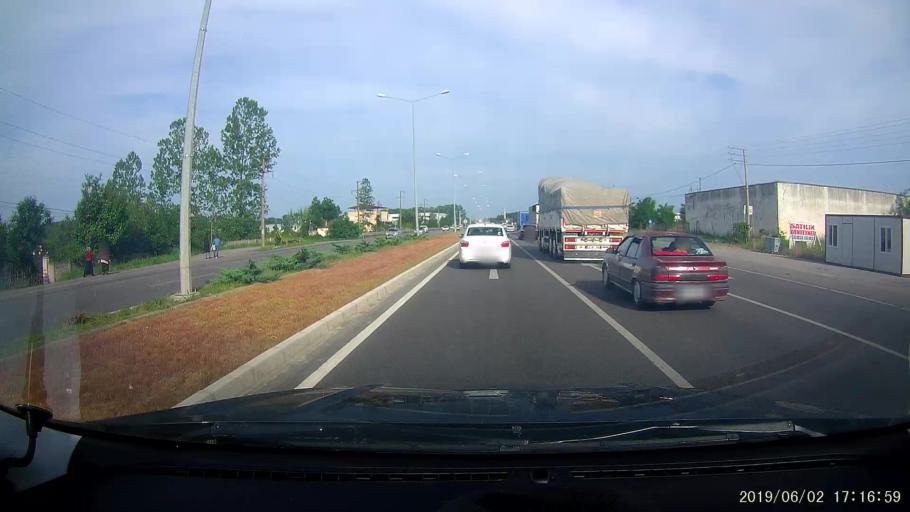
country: TR
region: Samsun
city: Dikbiyik
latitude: 41.2317
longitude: 36.5745
